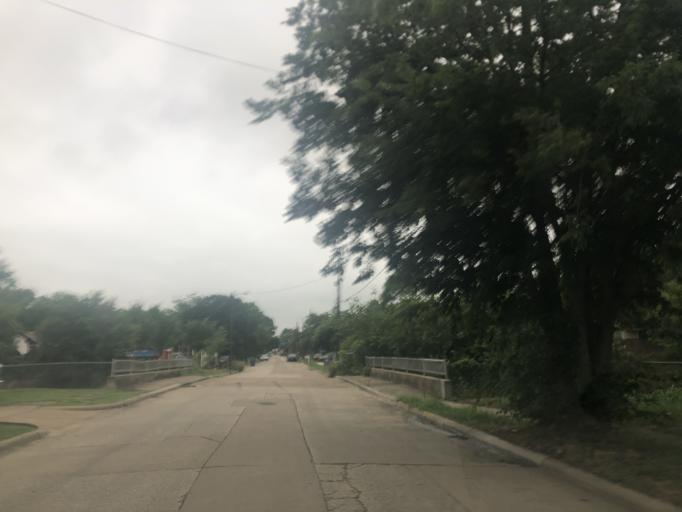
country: US
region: Texas
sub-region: Dallas County
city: Cockrell Hill
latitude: 32.7827
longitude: -96.8781
